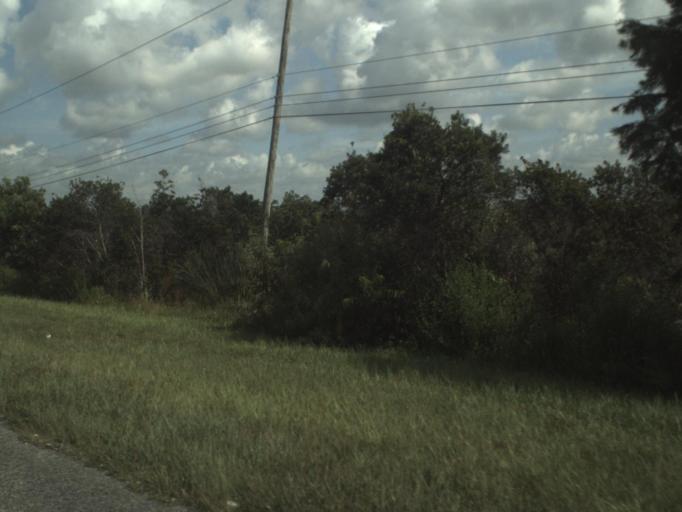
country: US
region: Florida
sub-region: Palm Beach County
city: Palm Beach Gardens
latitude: 26.8181
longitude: -80.1643
